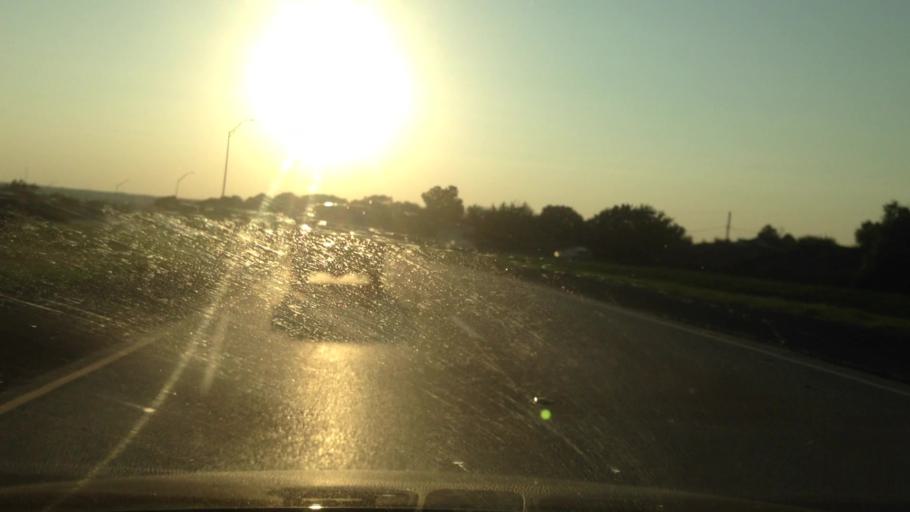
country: US
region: Texas
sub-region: Tarrant County
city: Kennedale
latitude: 32.6712
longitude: -97.2091
